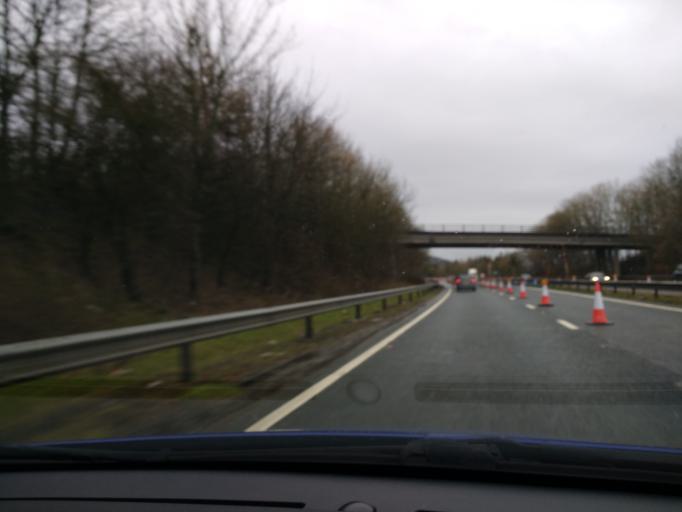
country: GB
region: England
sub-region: Cumbria
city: Milnthorpe
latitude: 54.2444
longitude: -2.7307
